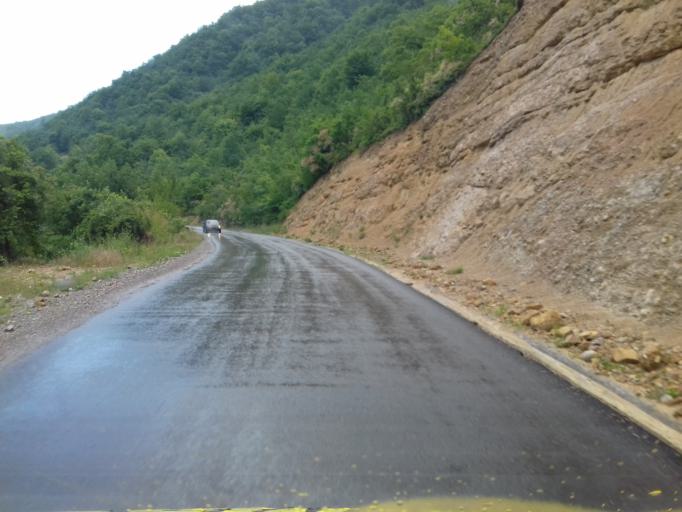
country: BA
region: Federation of Bosnia and Herzegovina
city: Visoko
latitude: 43.9553
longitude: 18.1482
